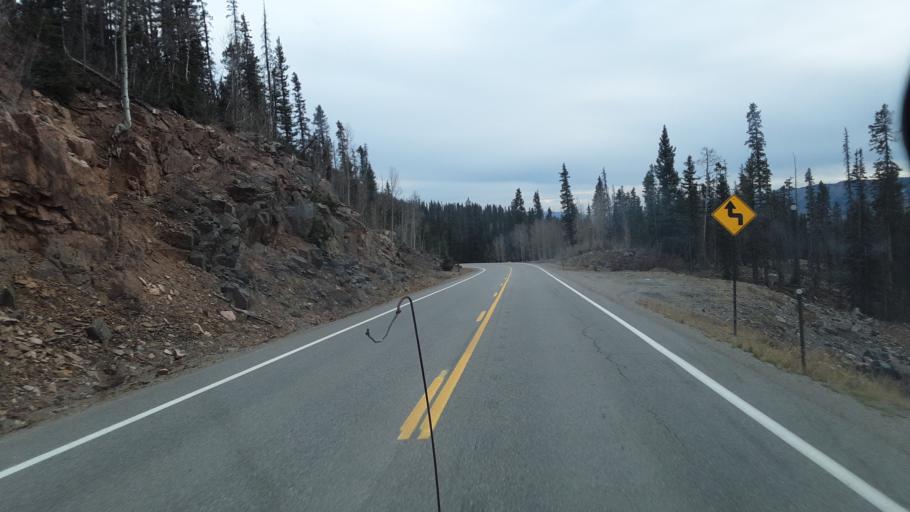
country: US
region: Colorado
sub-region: San Juan County
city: Silverton
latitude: 37.6848
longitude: -107.7794
